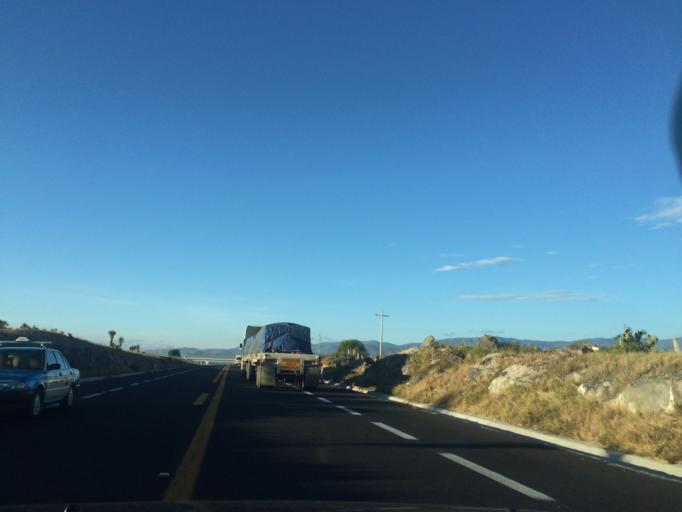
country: MX
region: Puebla
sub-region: Tehuacan
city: Magdalena Cuayucatepec
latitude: 18.5539
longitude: -97.4630
